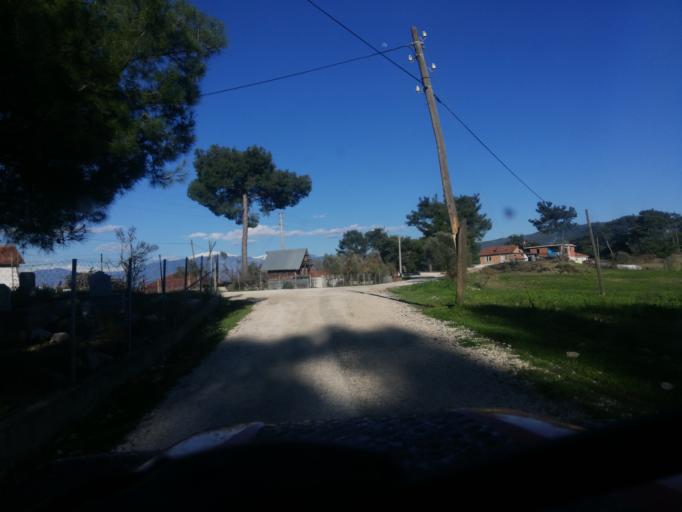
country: TR
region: Antalya
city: Kas
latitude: 36.2983
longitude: 29.6970
